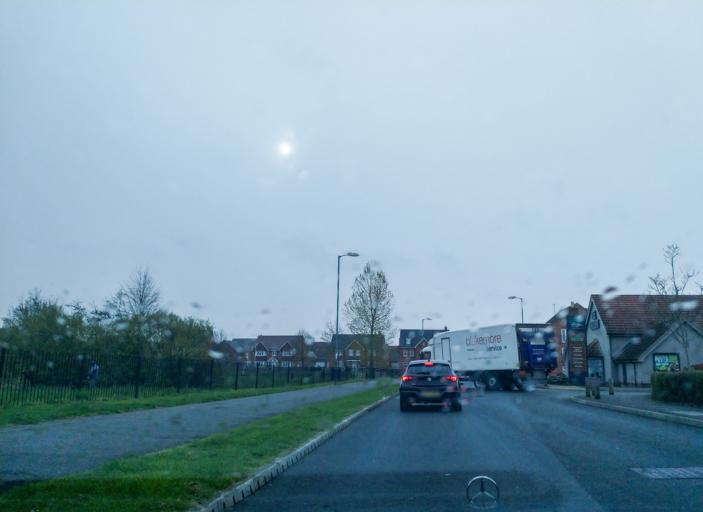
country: GB
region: England
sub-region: Warwickshire
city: Warwick
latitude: 52.2692
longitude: -1.6082
